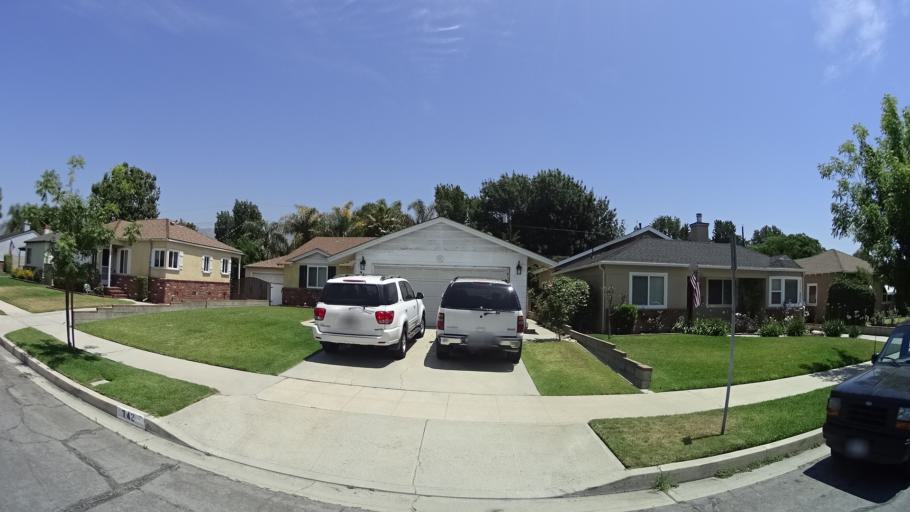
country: US
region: California
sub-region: Los Angeles County
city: Burbank
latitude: 34.1804
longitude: -118.3268
